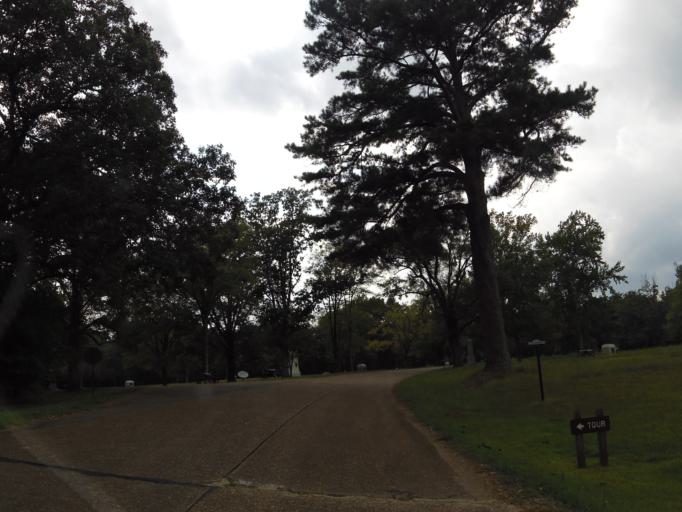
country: US
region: Tennessee
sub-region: Hardin County
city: Crump
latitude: 35.1376
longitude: -88.3493
